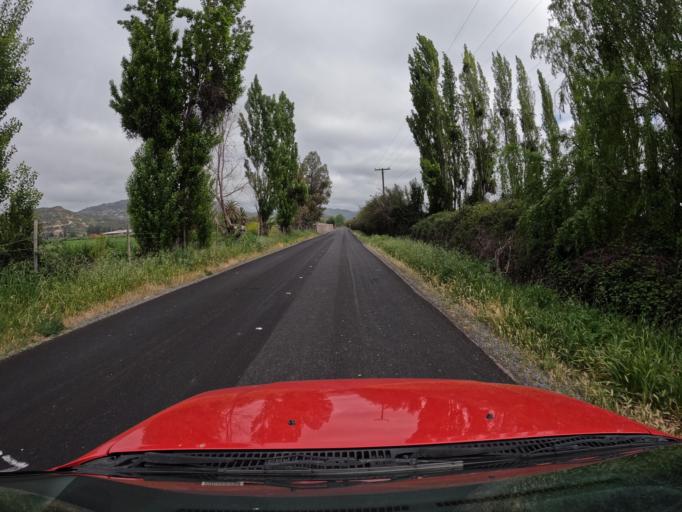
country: CL
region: O'Higgins
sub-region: Provincia de Colchagua
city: Santa Cruz
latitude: -34.6695
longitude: -71.3852
